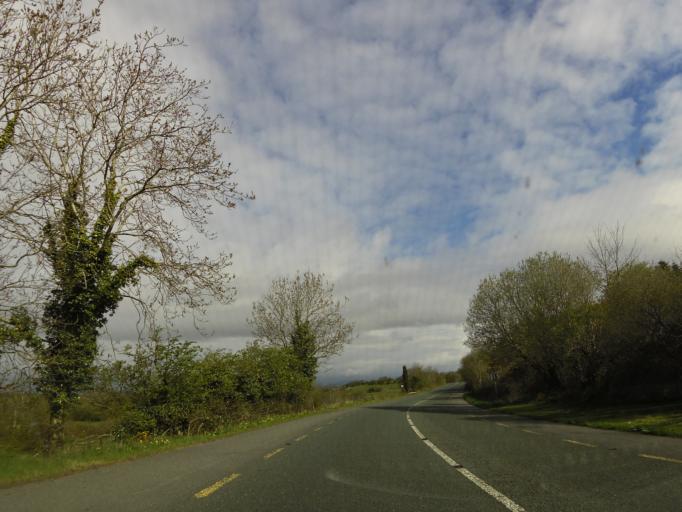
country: IE
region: Connaught
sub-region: Sligo
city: Tobercurry
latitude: 53.9388
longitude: -8.7905
